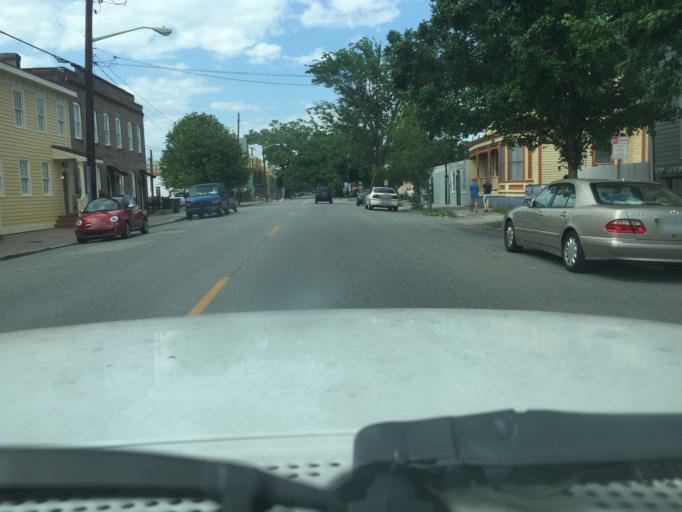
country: US
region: Georgia
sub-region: Chatham County
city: Savannah
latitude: 32.0694
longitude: -81.1002
